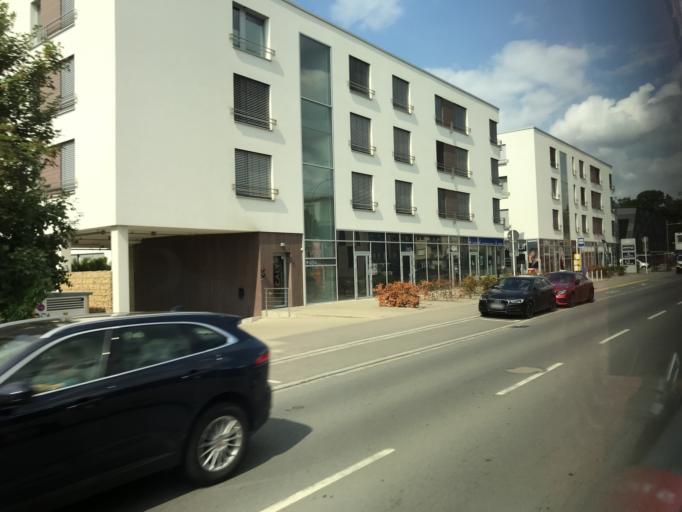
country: LU
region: Luxembourg
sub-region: Canton de Luxembourg
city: Alzingen
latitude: 49.5705
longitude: 6.1605
